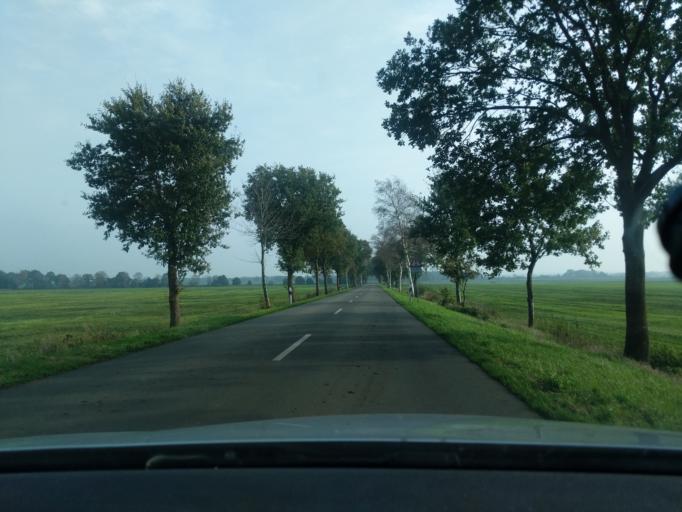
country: DE
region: Lower Saxony
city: Stinstedt
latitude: 53.6554
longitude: 8.9820
